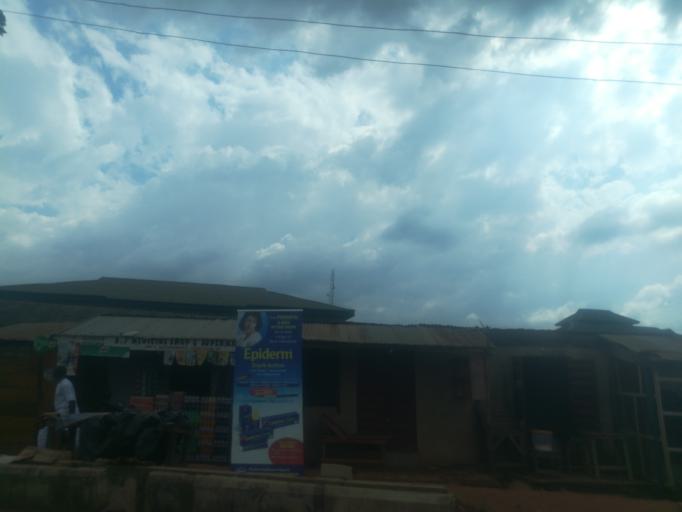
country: NG
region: Oyo
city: Ido
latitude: 7.4358
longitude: 3.8291
